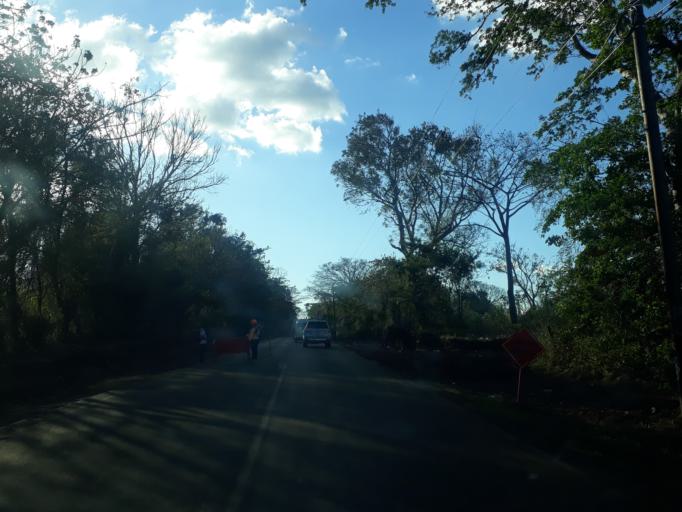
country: NI
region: Carazo
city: La Paz de Oriente
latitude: 11.8086
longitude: -86.1185
